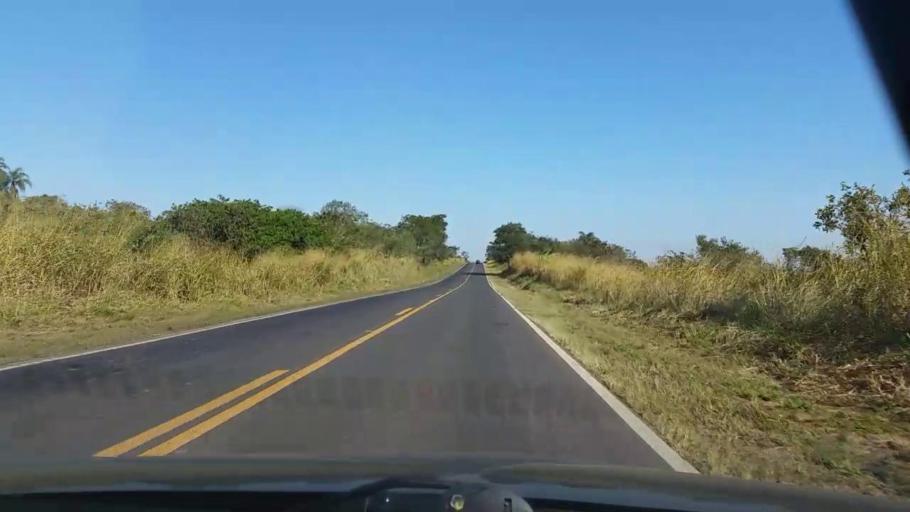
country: BR
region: Sao Paulo
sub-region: Itatinga
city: Itatinga
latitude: -22.8982
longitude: -48.7648
